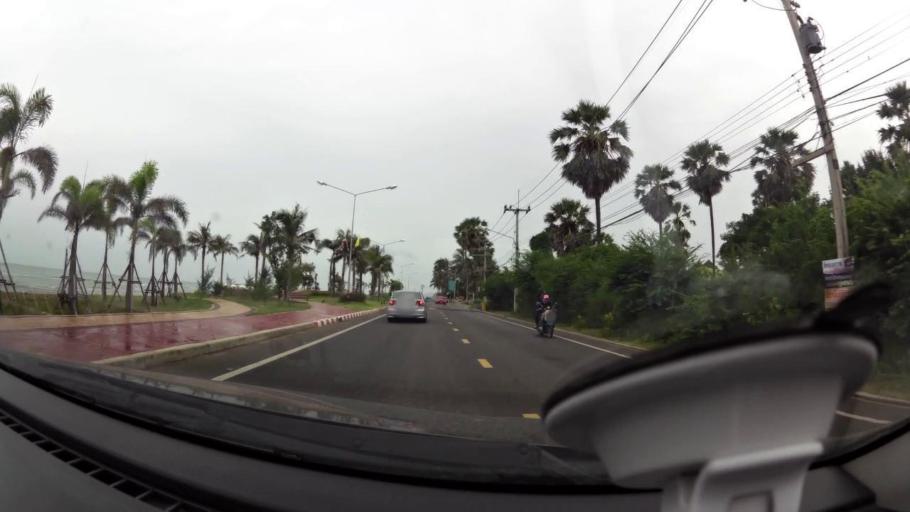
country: TH
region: Prachuap Khiri Khan
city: Pran Buri
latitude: 12.3793
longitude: 100.0000
